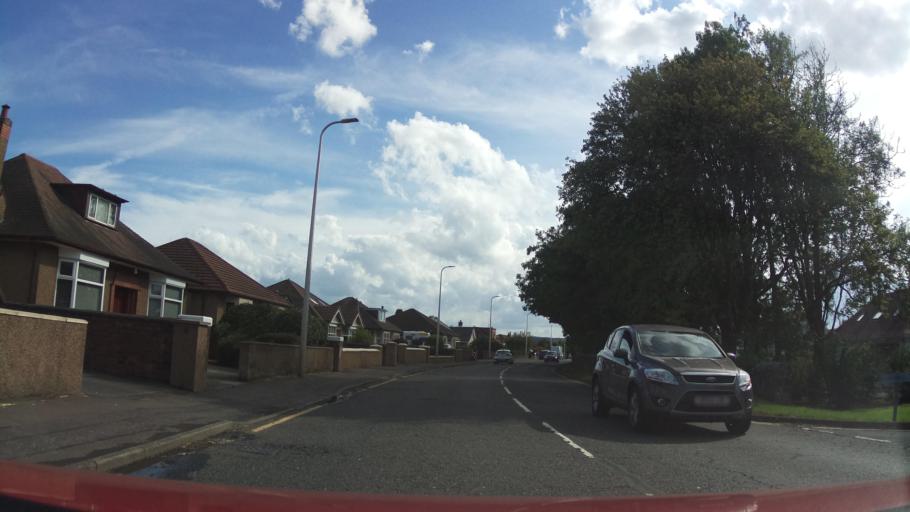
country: GB
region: Scotland
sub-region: Falkirk
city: Larbert
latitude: 56.0238
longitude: -3.8373
